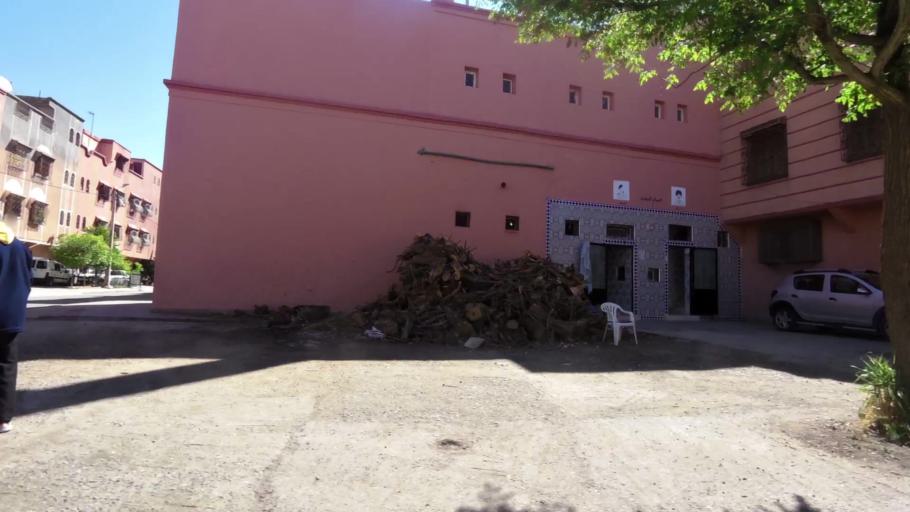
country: MA
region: Marrakech-Tensift-Al Haouz
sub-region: Marrakech
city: Marrakesh
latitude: 31.5949
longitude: -8.0467
